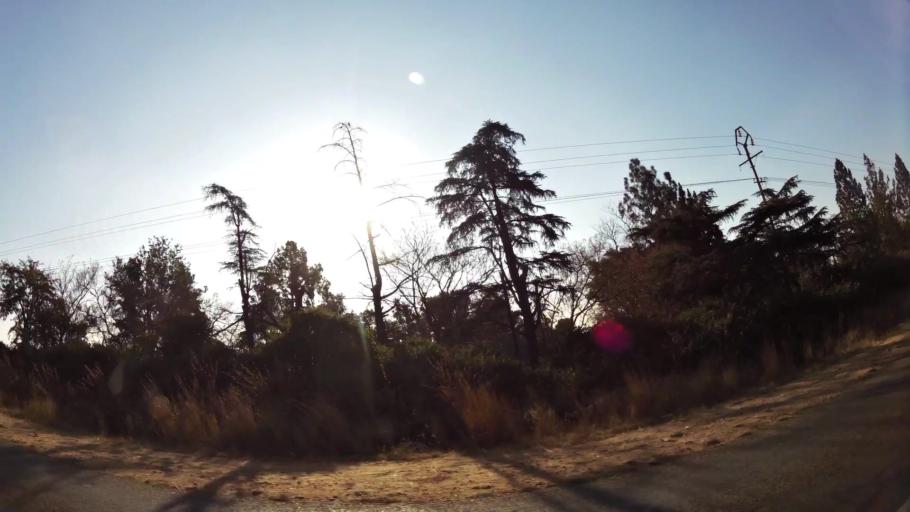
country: ZA
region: Gauteng
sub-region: West Rand District Municipality
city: Muldersdriseloop
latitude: -26.0170
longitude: 27.8847
